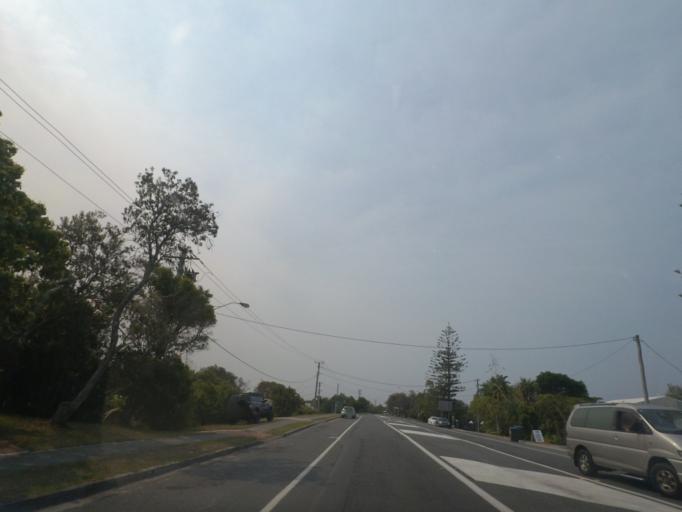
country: AU
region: New South Wales
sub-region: Tweed
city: Casuarina
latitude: -28.3300
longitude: 153.5689
